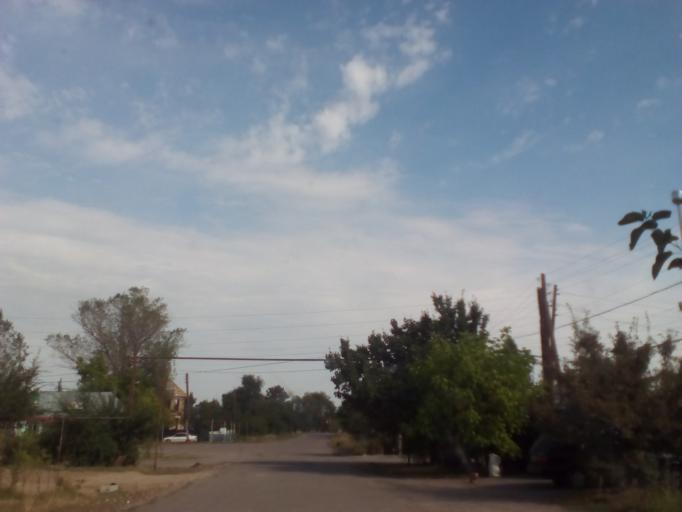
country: KZ
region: Almaty Oblysy
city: Burunday
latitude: 43.1677
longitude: 76.4047
